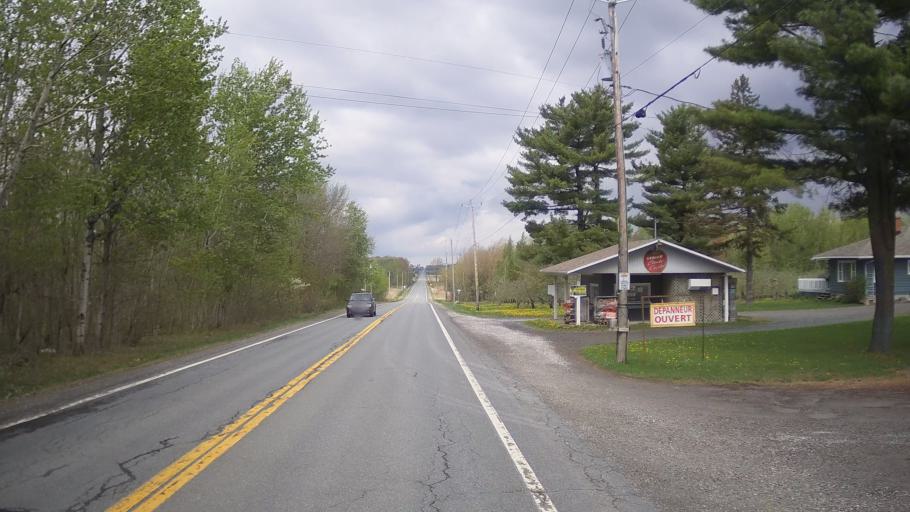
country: CA
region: Quebec
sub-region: Monteregie
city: Farnham
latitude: 45.2480
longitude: -72.8944
